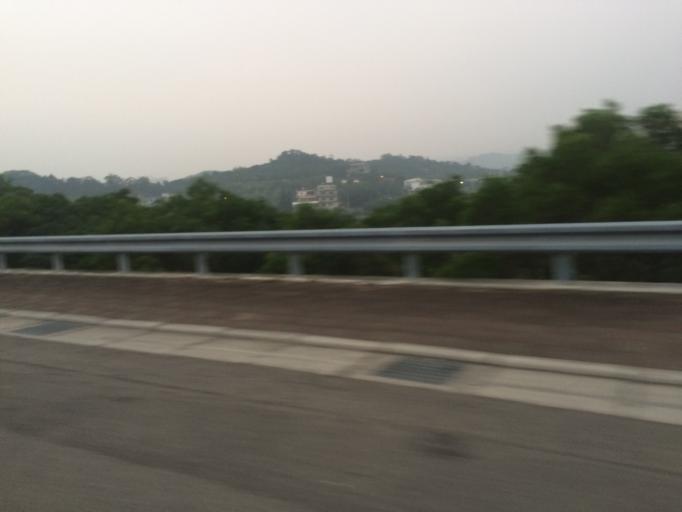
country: TW
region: Taiwan
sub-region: Hsinchu
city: Hsinchu
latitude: 24.7167
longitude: 120.9177
